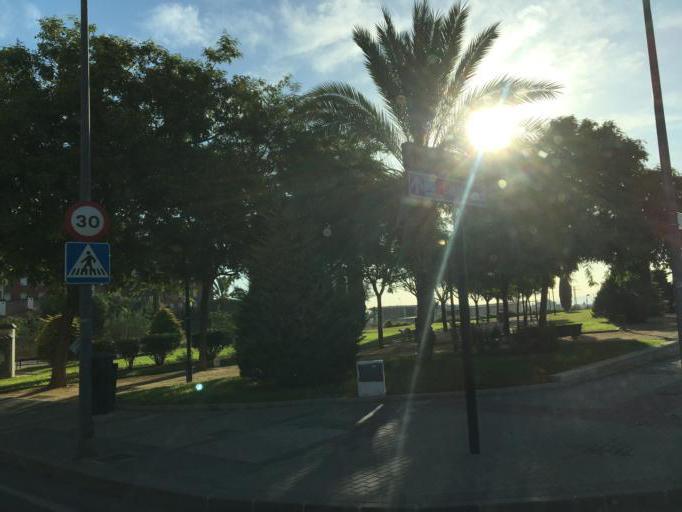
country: ES
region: Murcia
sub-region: Murcia
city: Murcia
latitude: 38.0131
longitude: -1.1510
